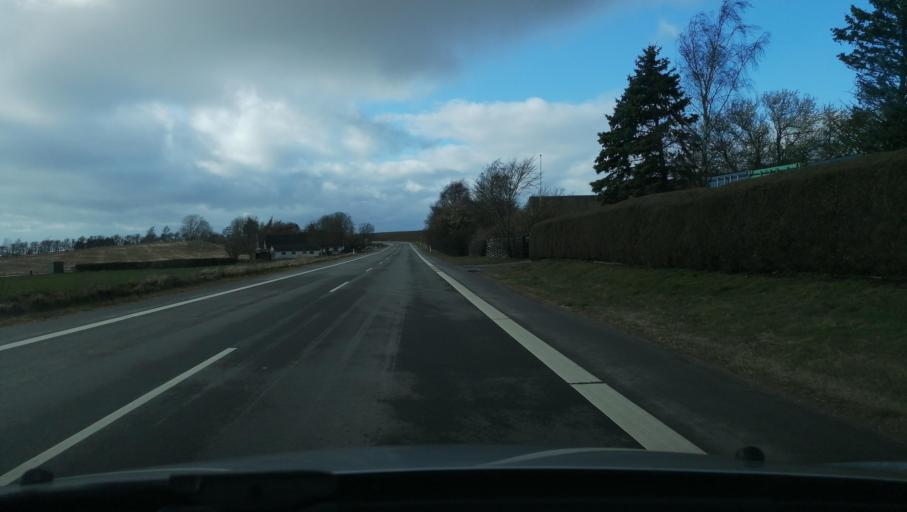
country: DK
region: Zealand
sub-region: Odsherred Kommune
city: Horve
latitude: 55.7619
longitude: 11.4413
